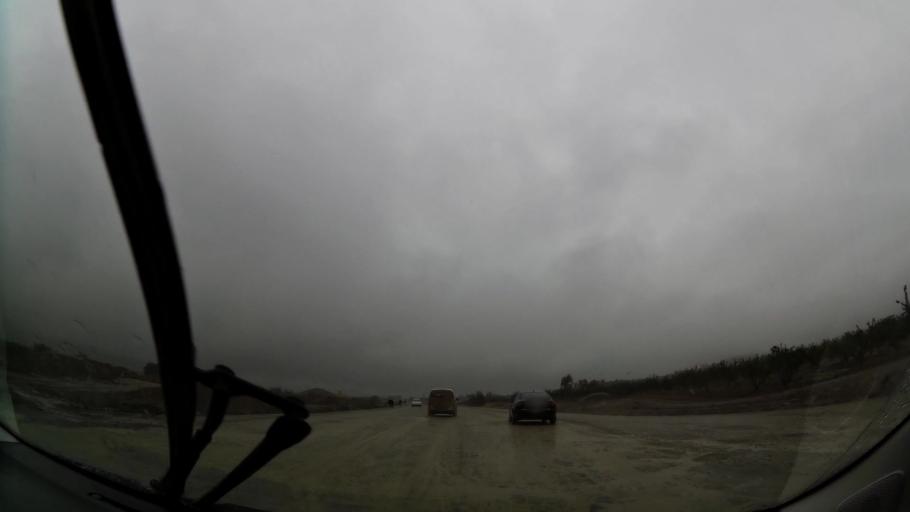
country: MA
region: Oriental
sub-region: Nador
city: Midar
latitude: 34.8686
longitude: -3.7257
